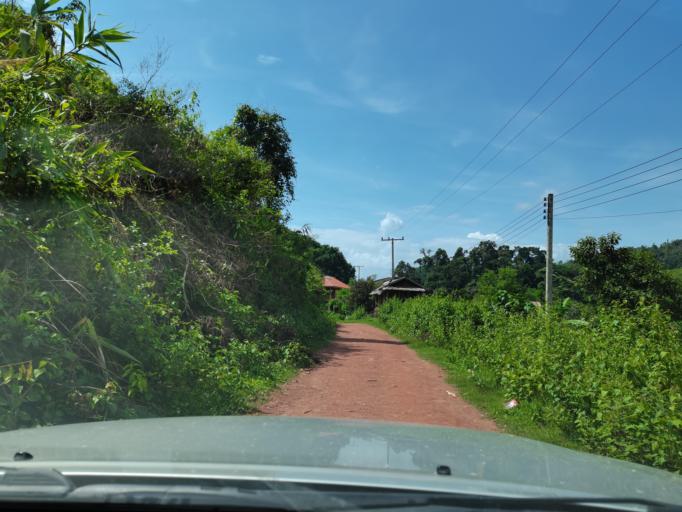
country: LA
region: Loungnamtha
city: Muang Nale
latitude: 20.5284
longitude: 101.0649
